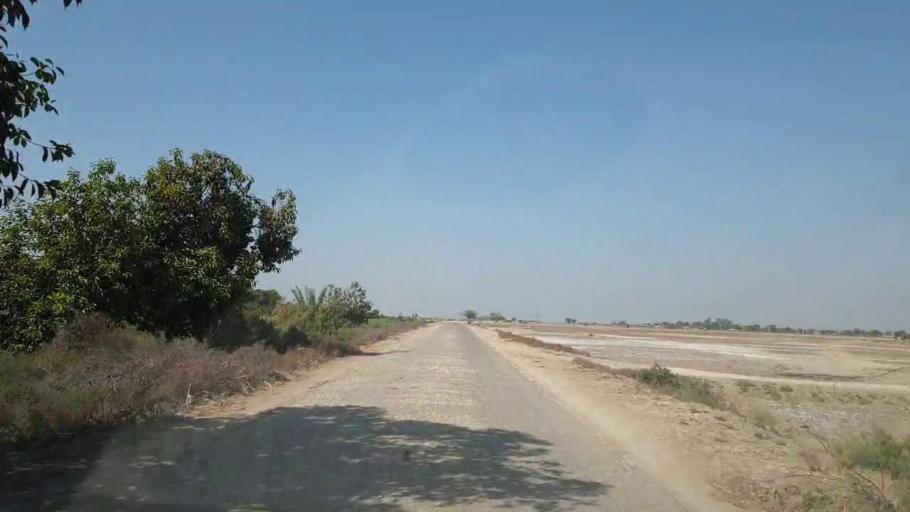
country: PK
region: Sindh
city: Mirpur Khas
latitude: 25.6708
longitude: 69.1089
